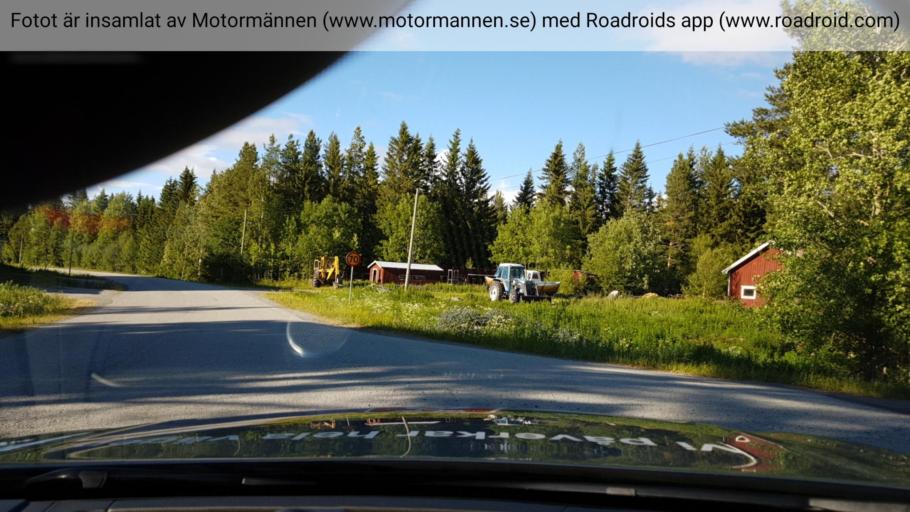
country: SE
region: Jaemtland
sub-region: Bergs Kommun
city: Hoverberg
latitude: 62.9432
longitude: 14.3827
